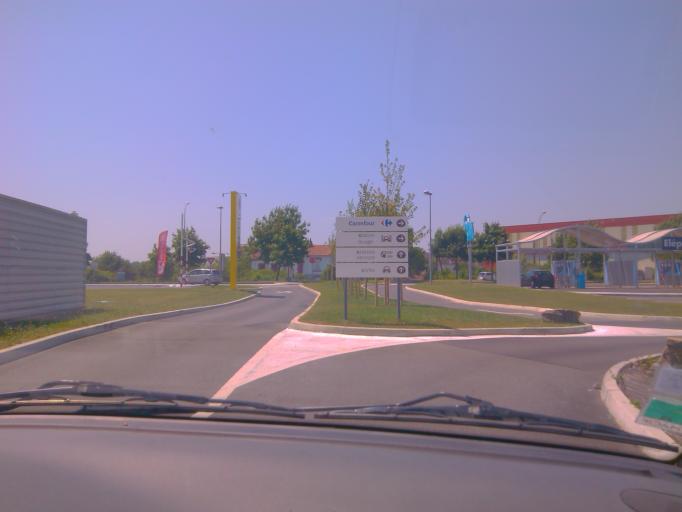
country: FR
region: Bourgogne
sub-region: Departement de Saone-et-Loire
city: Chalon-sur-Saone
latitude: 46.7732
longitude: 4.8602
